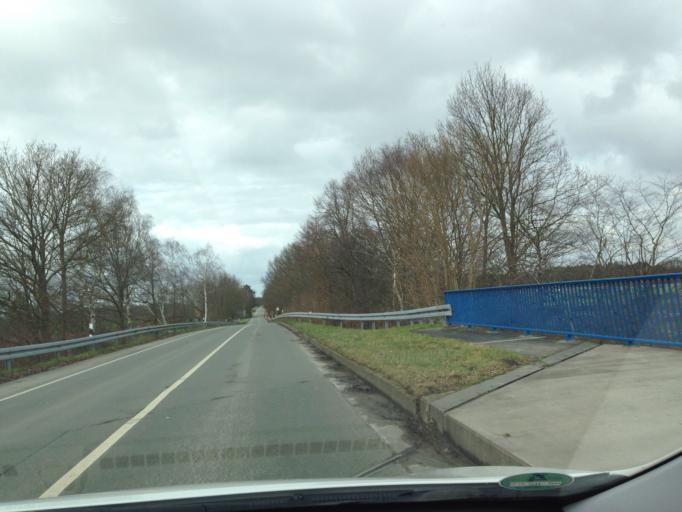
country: DE
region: North Rhine-Westphalia
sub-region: Regierungsbezirk Munster
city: Greven
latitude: 52.0270
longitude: 7.5991
